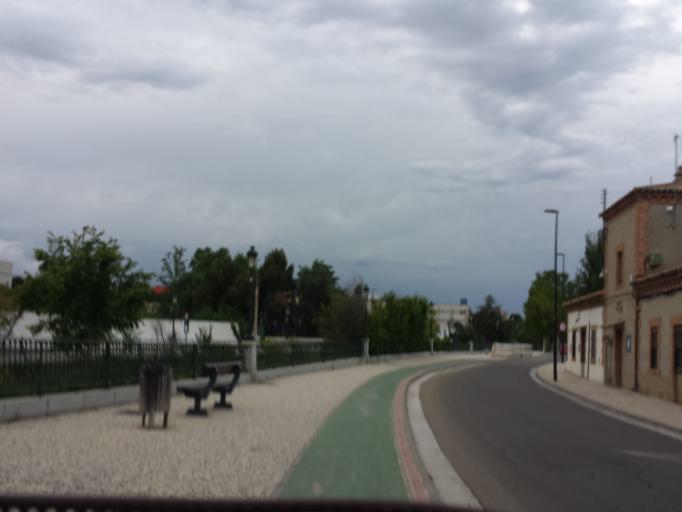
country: ES
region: Aragon
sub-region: Provincia de Zaragoza
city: Delicias
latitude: 41.6220
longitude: -0.9046
